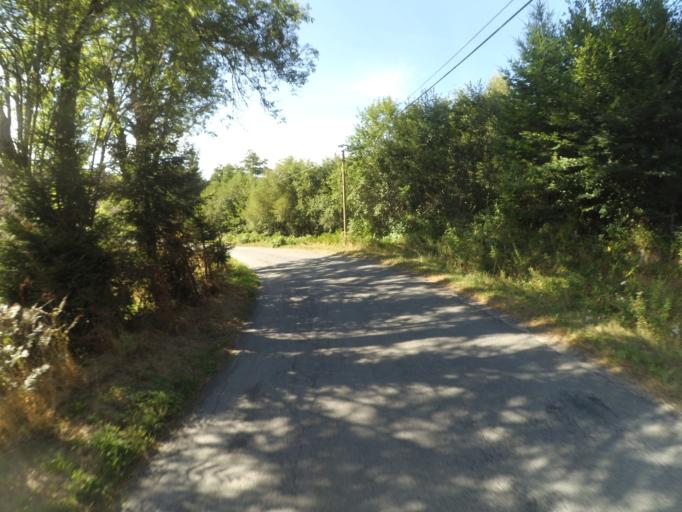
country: FR
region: Limousin
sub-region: Departement de la Correze
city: Bugeat
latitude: 45.6838
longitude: 1.9390
